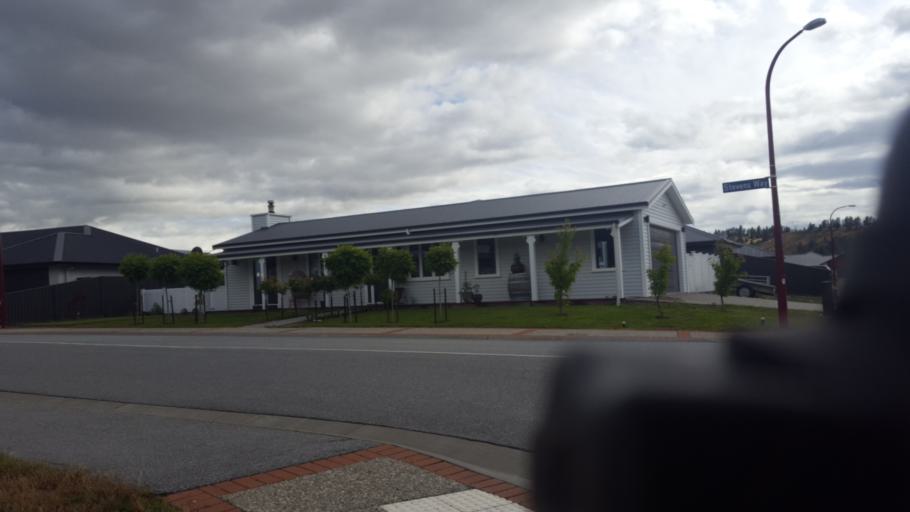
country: NZ
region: Otago
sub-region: Queenstown-Lakes District
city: Wanaka
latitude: -45.2420
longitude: 169.3790
